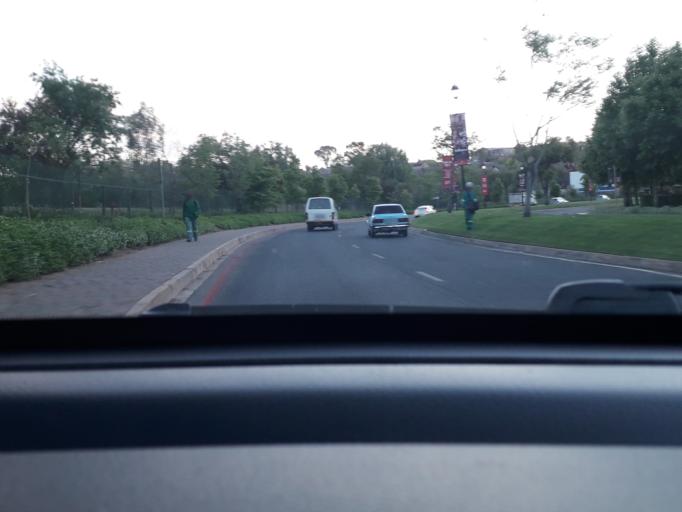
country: ZA
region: Gauteng
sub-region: City of Johannesburg Metropolitan Municipality
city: Diepsloot
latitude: -26.0256
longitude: 28.0163
